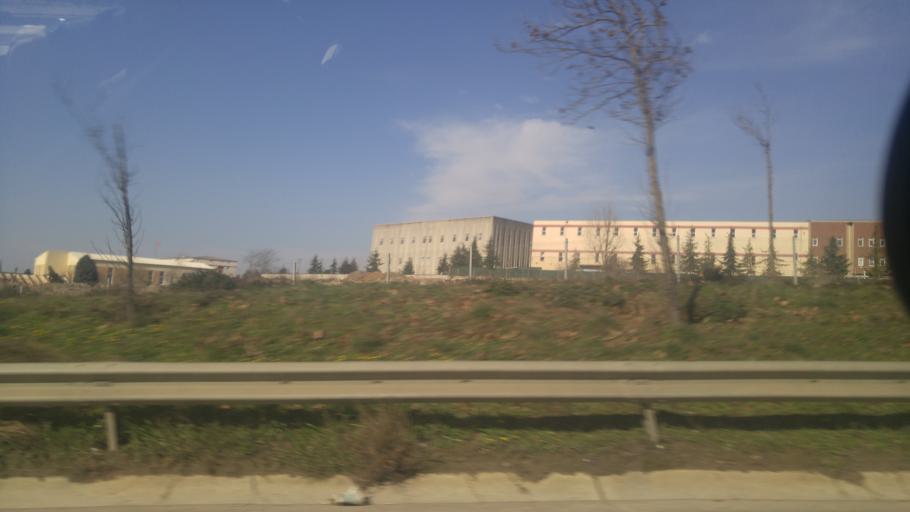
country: TR
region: Kocaeli
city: Balcik
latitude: 40.8562
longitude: 29.3760
